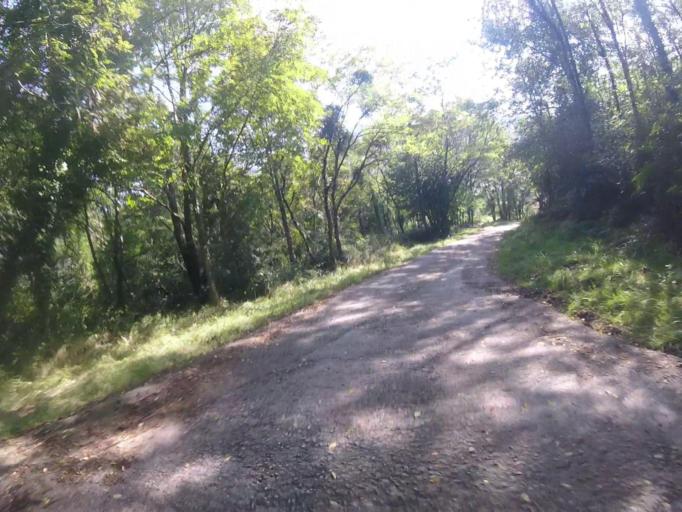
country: ES
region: Basque Country
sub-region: Provincia de Guipuzcoa
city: Irun
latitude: 43.3231
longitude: -1.7451
